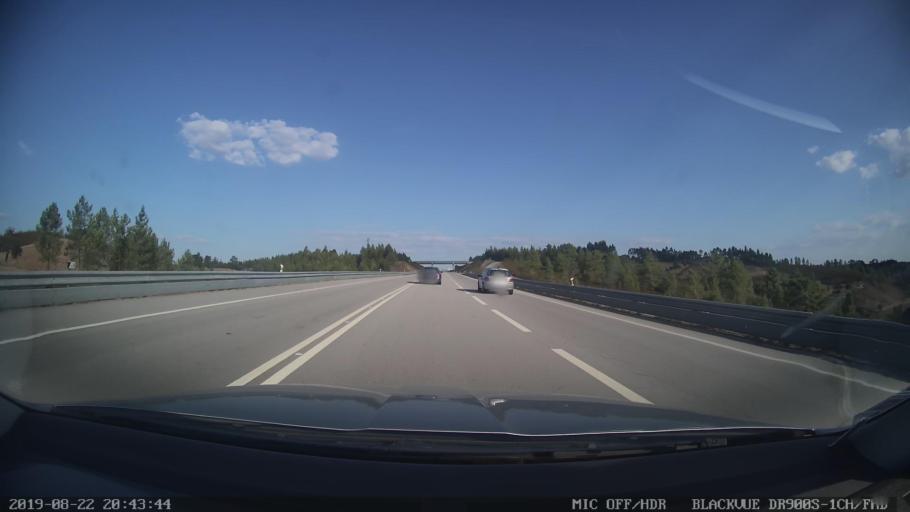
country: PT
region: Castelo Branco
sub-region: Proenca-A-Nova
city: Proenca-a-Nova
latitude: 39.7008
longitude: -7.8378
